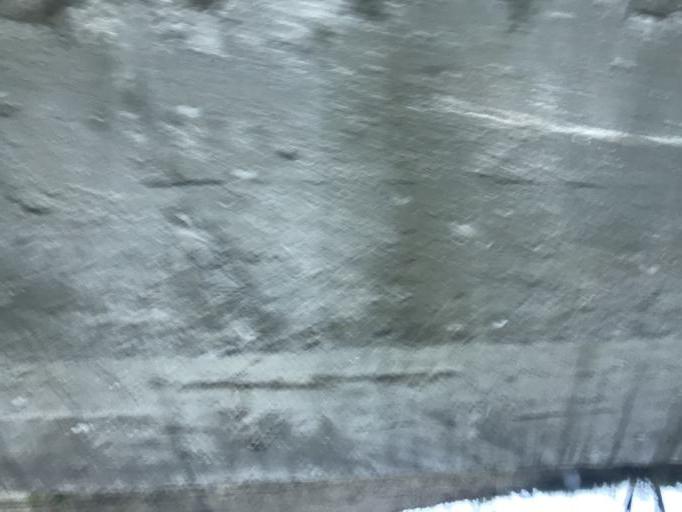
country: GT
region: Chimaltenango
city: Parramos
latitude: 14.6255
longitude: -90.8041
